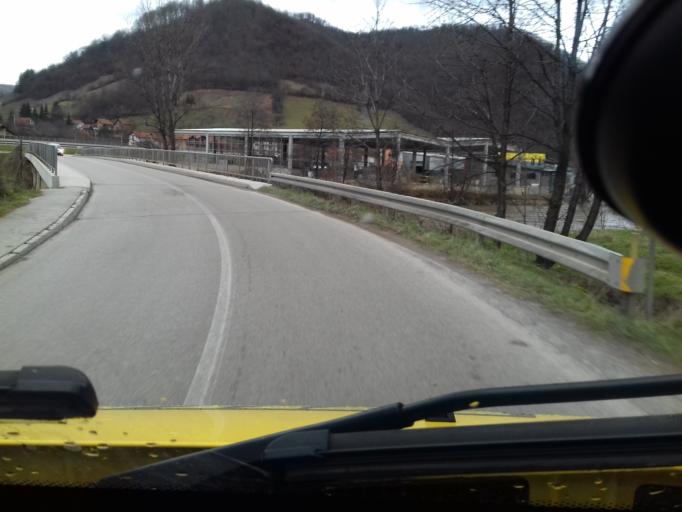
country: BA
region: Federation of Bosnia and Herzegovina
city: Dobrinje
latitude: 44.0546
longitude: 18.1061
